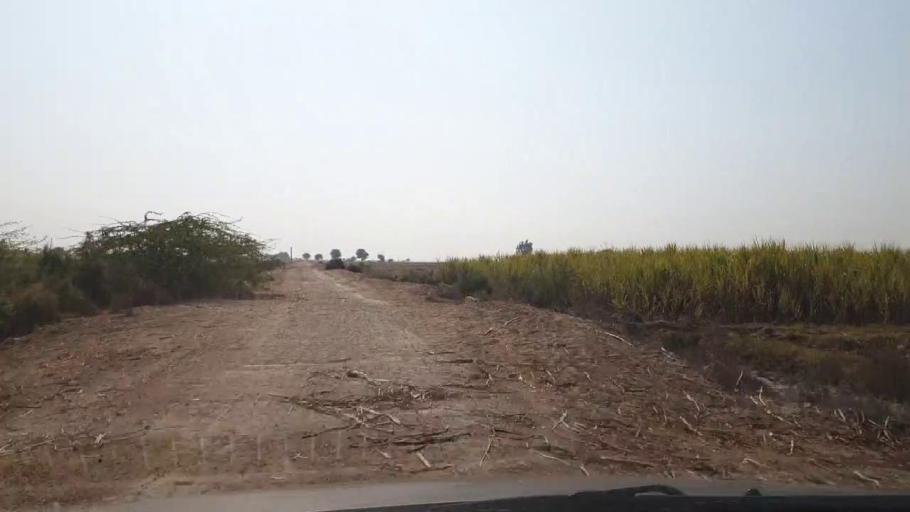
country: PK
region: Sindh
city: Jhol
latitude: 25.8652
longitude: 68.9981
